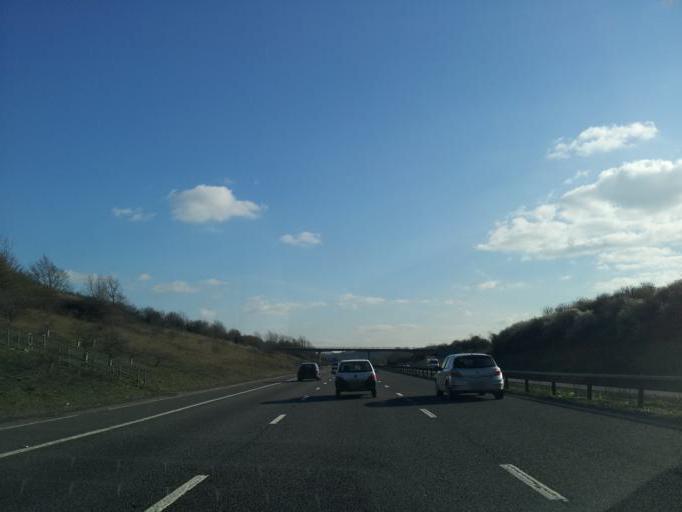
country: GB
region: England
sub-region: North Somerset
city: St. Georges
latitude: 51.3422
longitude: -2.8946
